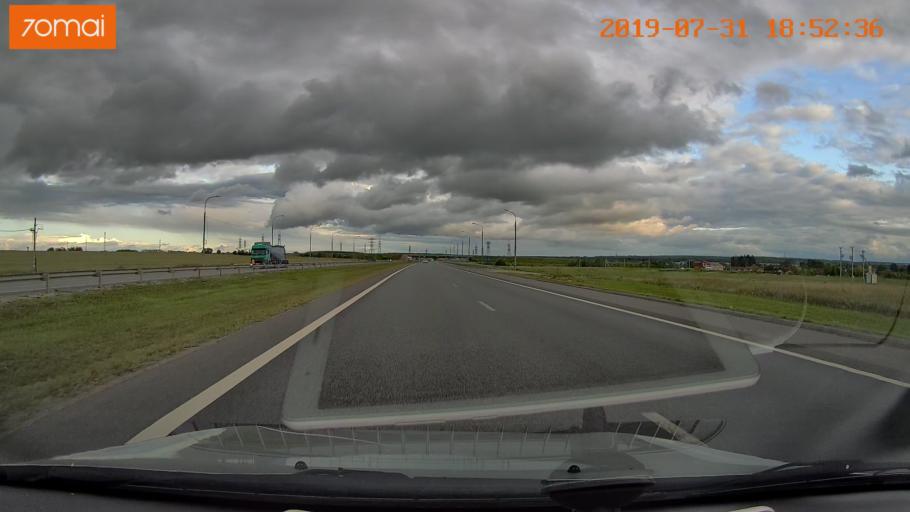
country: RU
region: Moskovskaya
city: Voskresensk
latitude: 55.2122
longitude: 38.6355
